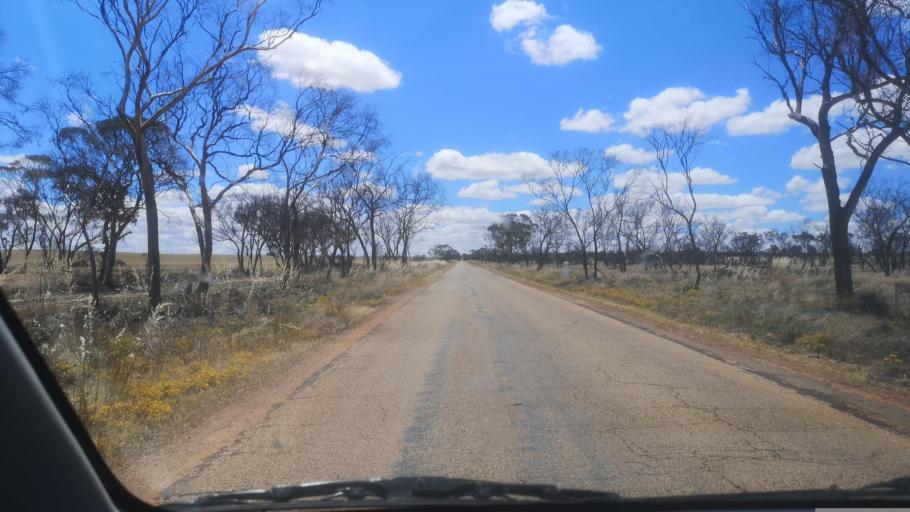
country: AU
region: Western Australia
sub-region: Cunderdin
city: Cunderdin
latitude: -32.1877
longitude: 117.6598
